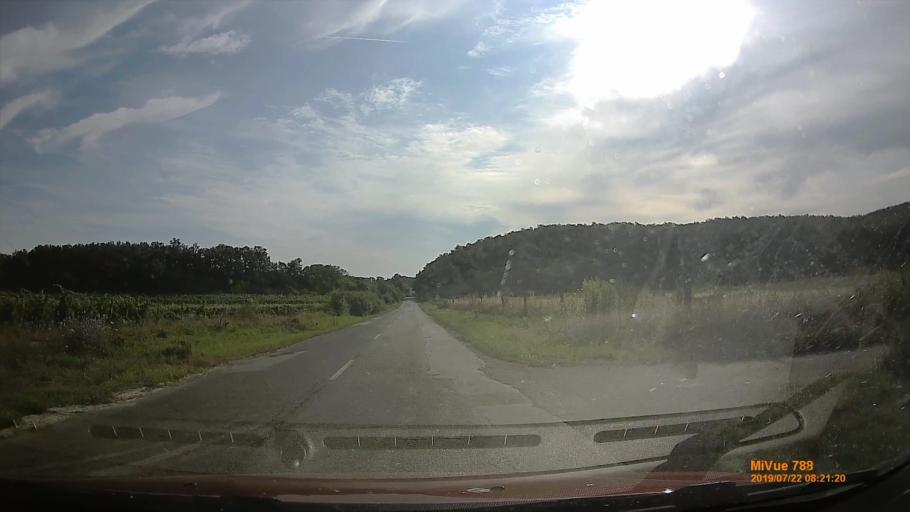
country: HU
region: Veszprem
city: Balatonfured
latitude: 46.9650
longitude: 17.8396
